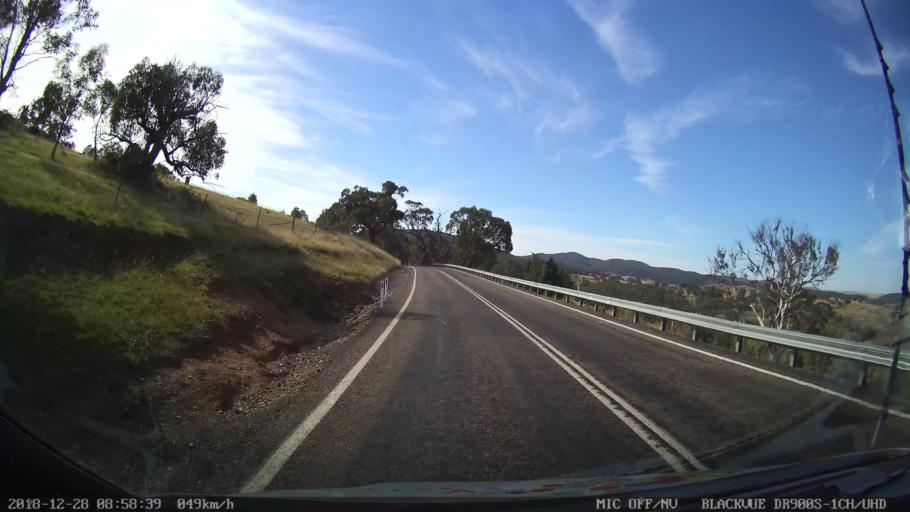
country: AU
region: New South Wales
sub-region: Upper Lachlan Shire
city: Crookwell
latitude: -34.1287
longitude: 149.3321
